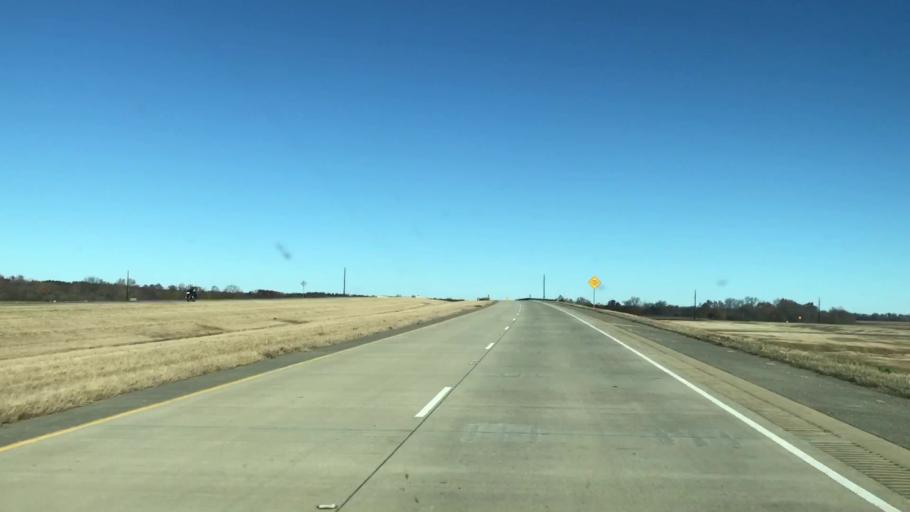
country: US
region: Louisiana
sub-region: Caddo Parish
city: Vivian
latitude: 32.8944
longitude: -93.8605
